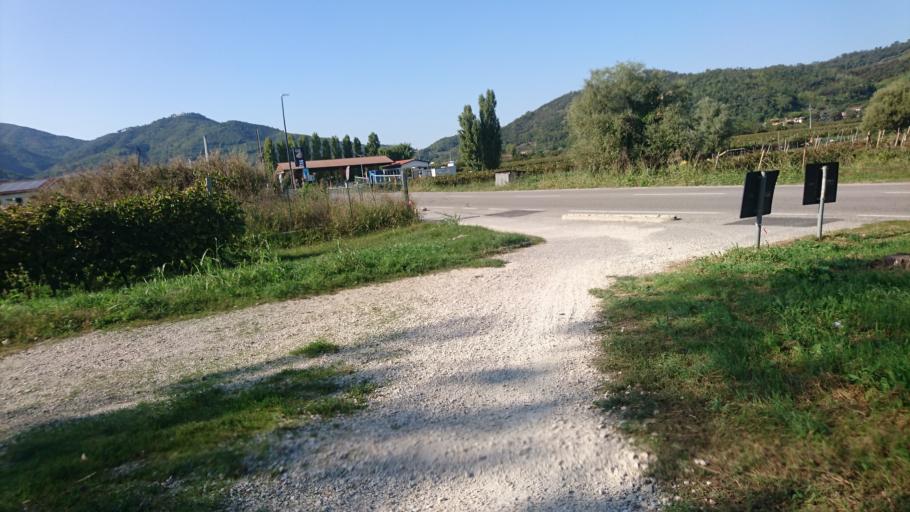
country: IT
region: Veneto
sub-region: Provincia di Padova
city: Galzignano
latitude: 45.3029
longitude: 11.7479
